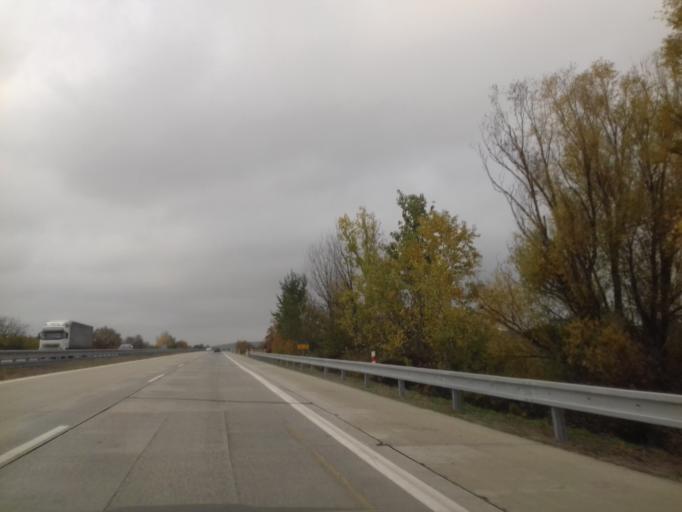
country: CZ
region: South Moravian
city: Velke Pavlovice
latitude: 48.9107
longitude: 16.7790
